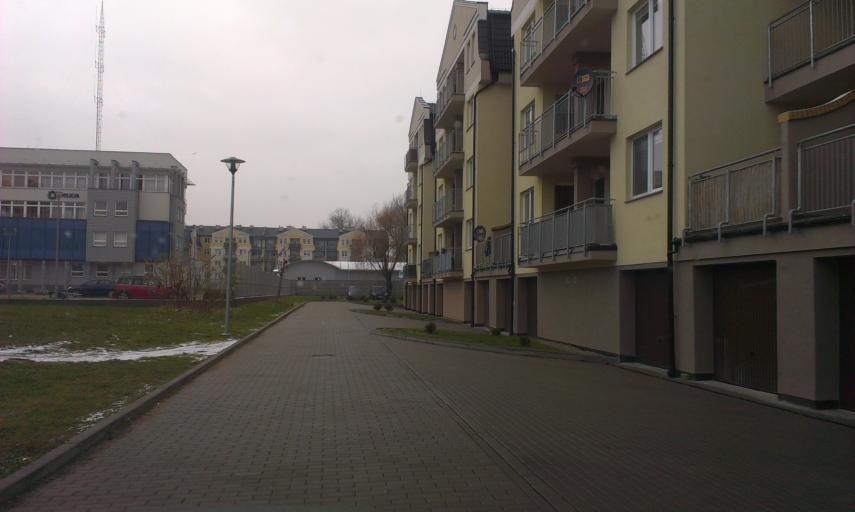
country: PL
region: West Pomeranian Voivodeship
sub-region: Powiat szczecinecki
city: Szczecinek
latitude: 53.7169
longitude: 16.6791
